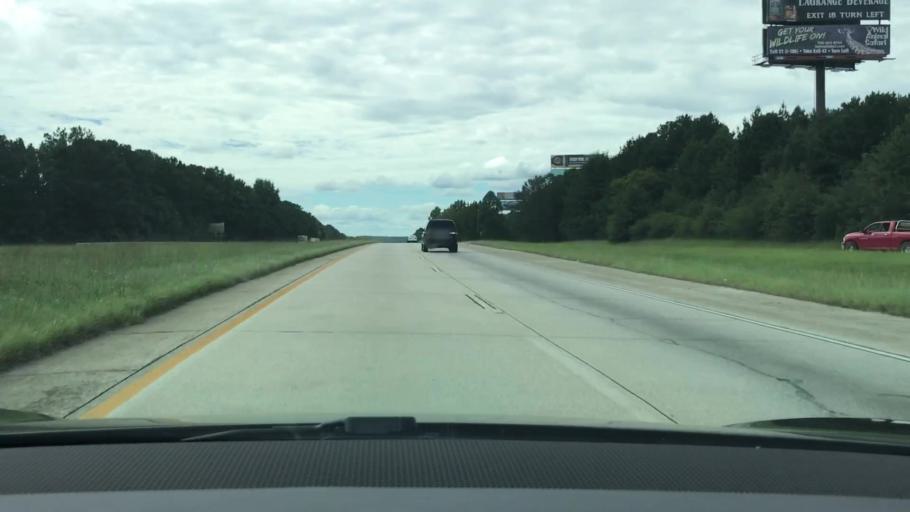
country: US
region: Georgia
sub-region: Troup County
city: Hogansville
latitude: 33.1569
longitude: -84.8705
